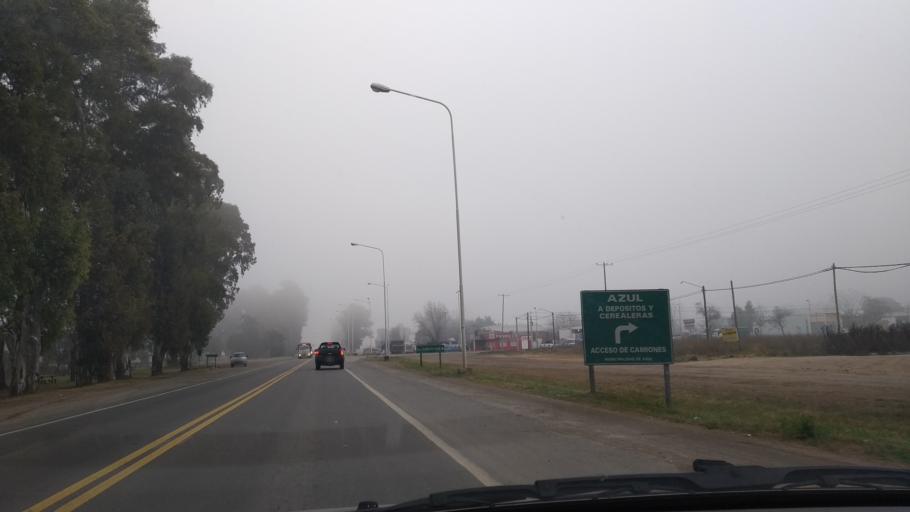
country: AR
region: Buenos Aires
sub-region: Partido de Azul
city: Azul
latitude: -36.7957
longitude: -59.8449
